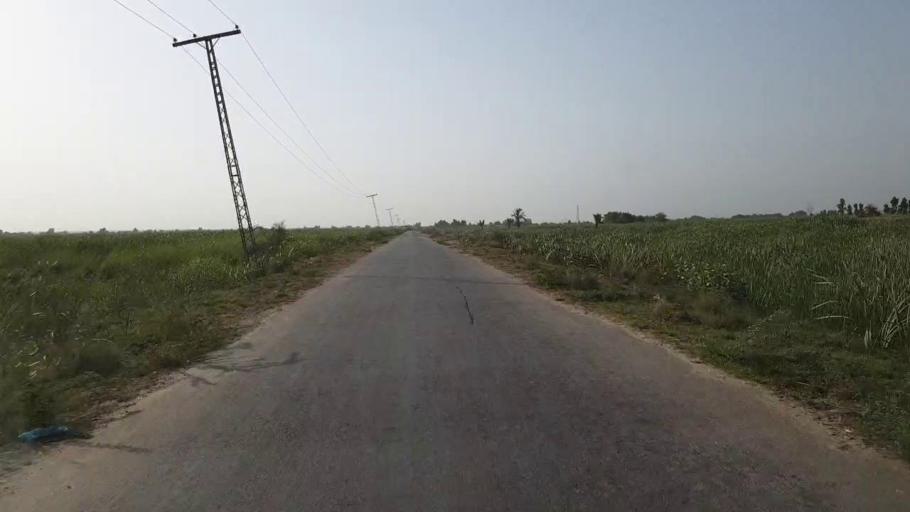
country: PK
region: Sindh
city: Jam Sahib
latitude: 26.4134
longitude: 68.8735
